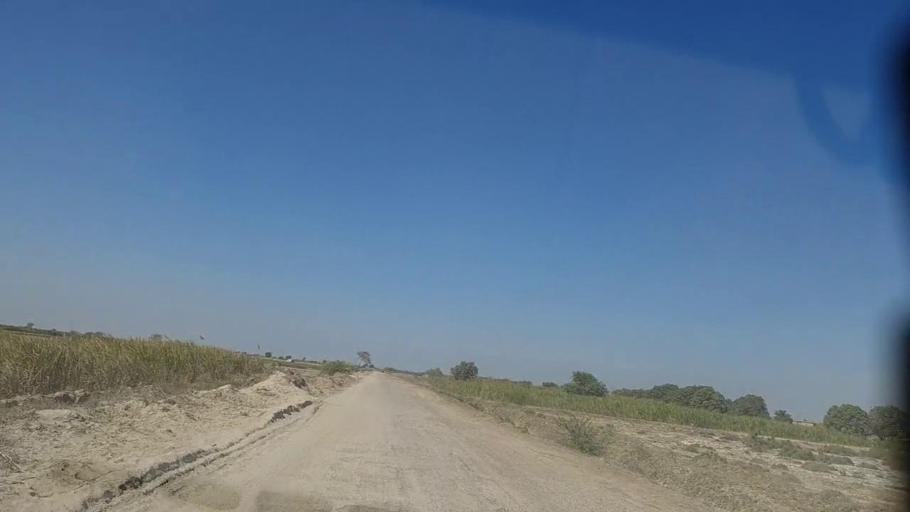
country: PK
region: Sindh
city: Mirwah Gorchani
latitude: 25.2241
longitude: 69.0216
